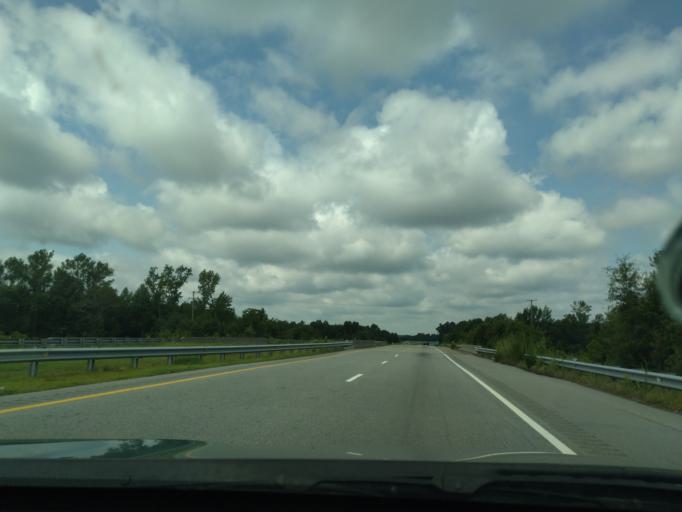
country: US
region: North Carolina
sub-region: Martin County
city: Robersonville
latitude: 35.8267
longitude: -77.1694
